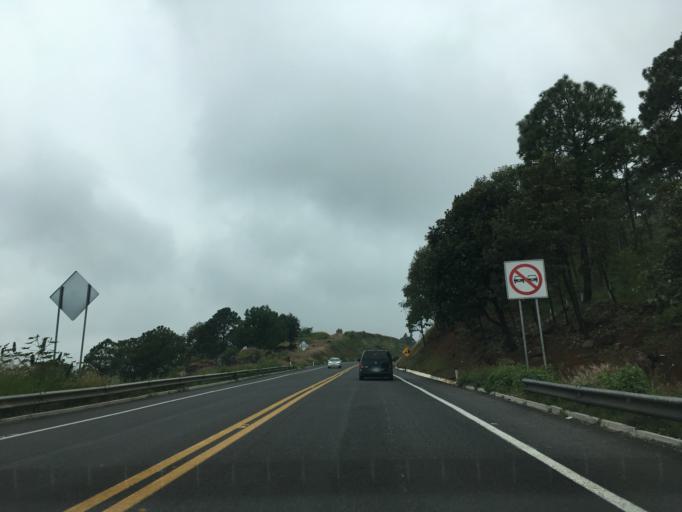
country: MX
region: Michoacan
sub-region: Uruapan
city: Toreo Bajo (El Toreo Bajo)
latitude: 19.4159
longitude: -101.9723
